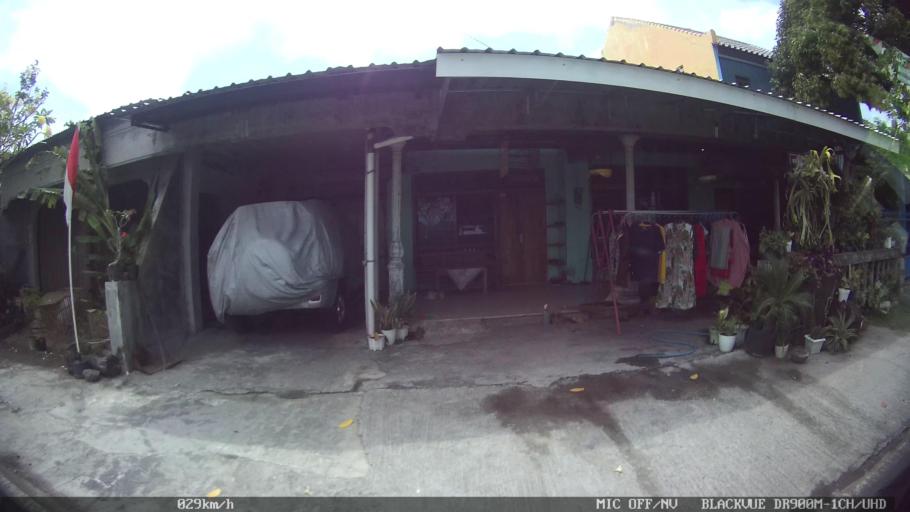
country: ID
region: Daerah Istimewa Yogyakarta
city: Depok
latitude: -7.8097
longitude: 110.4432
